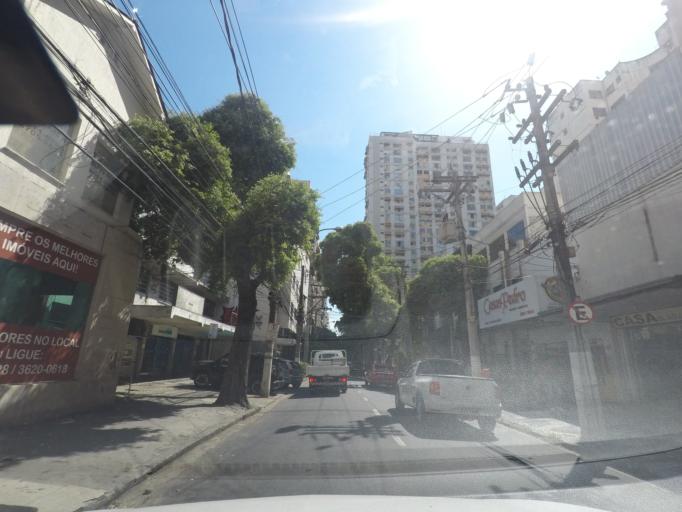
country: BR
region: Rio de Janeiro
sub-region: Niteroi
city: Niteroi
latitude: -22.9023
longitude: -43.1108
